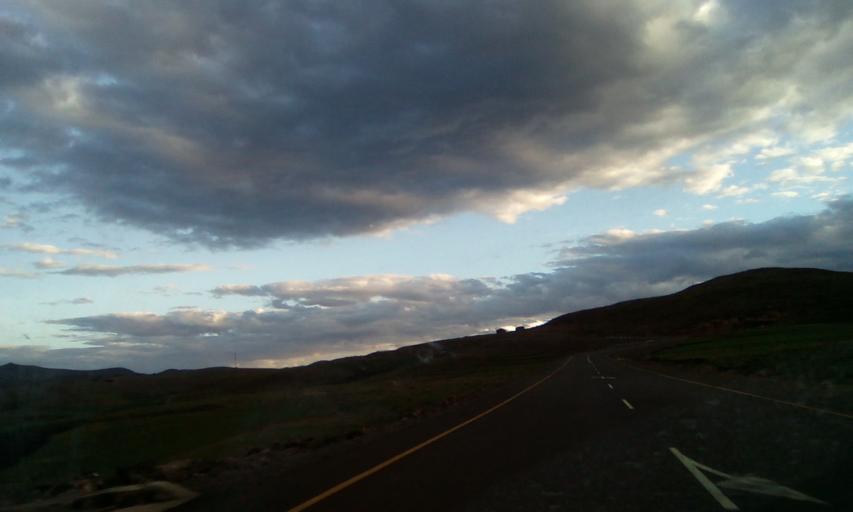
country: LS
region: Maseru
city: Nako
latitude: -29.8112
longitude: 28.0325
